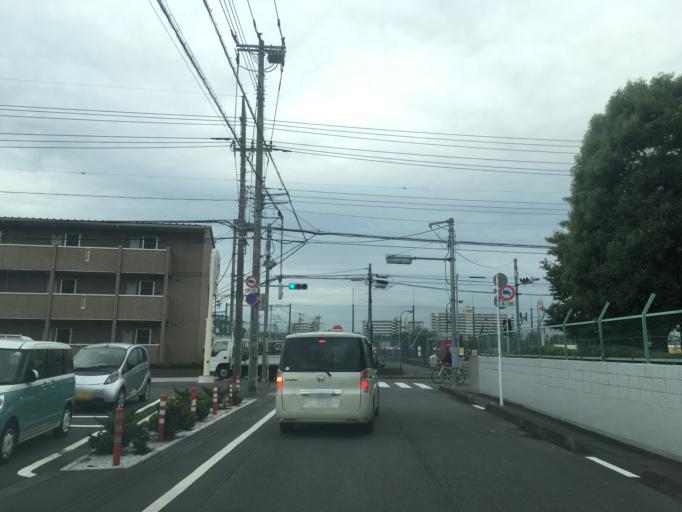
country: JP
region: Tokyo
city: Higashimurayama-shi
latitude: 35.7569
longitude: 139.4604
